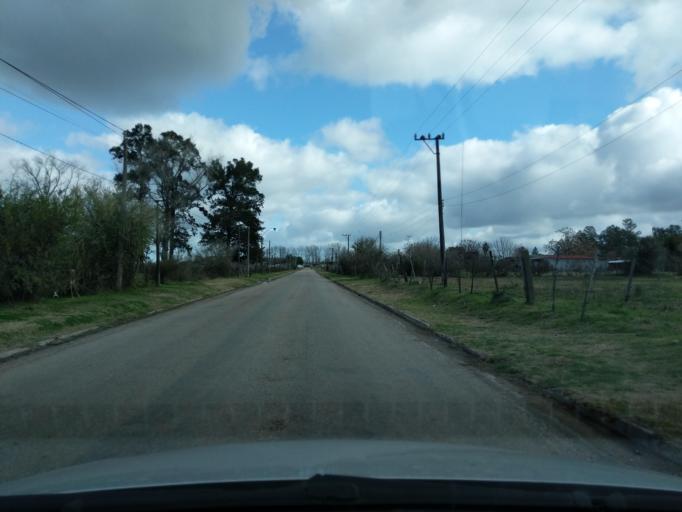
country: UY
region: Florida
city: Florida
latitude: -34.1085
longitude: -56.2194
